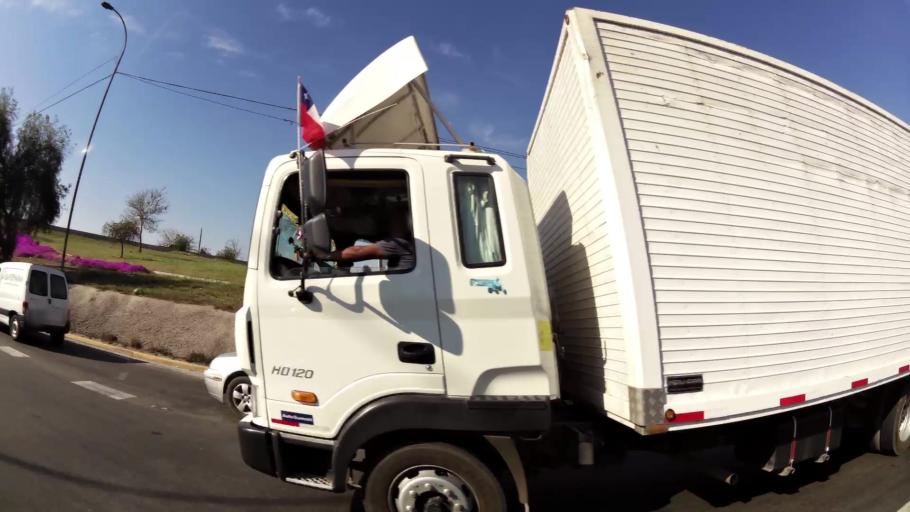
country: CL
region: Santiago Metropolitan
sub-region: Provincia de Santiago
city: Lo Prado
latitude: -33.4467
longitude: -70.7774
